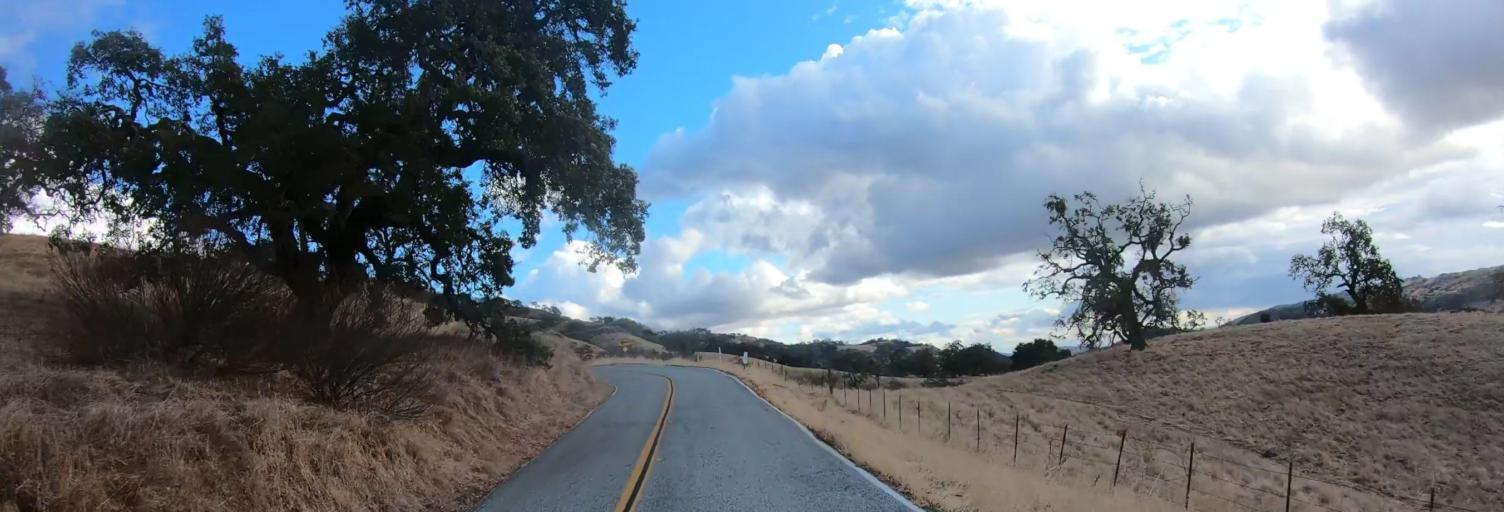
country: US
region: California
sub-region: Santa Clara County
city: East Foothills
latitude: 37.3348
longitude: -121.7023
